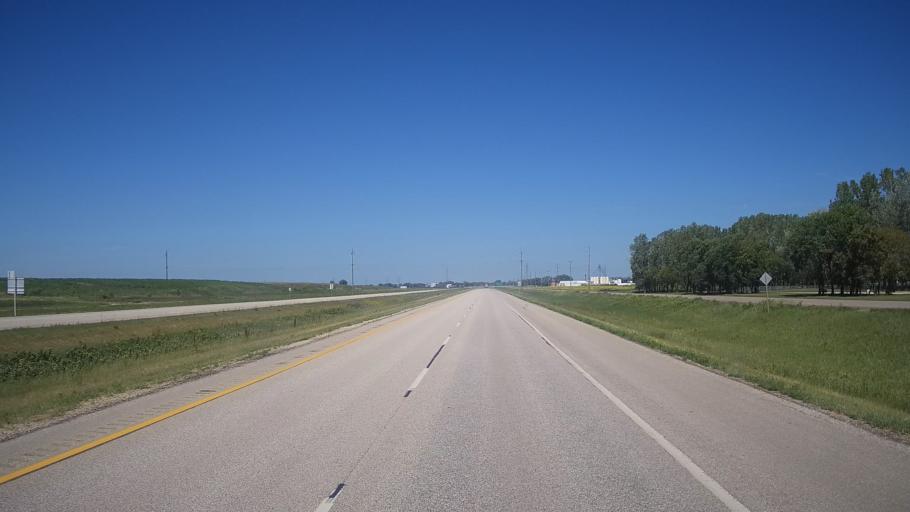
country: CA
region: Manitoba
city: Portage la Prairie
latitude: 49.9557
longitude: -98.3313
